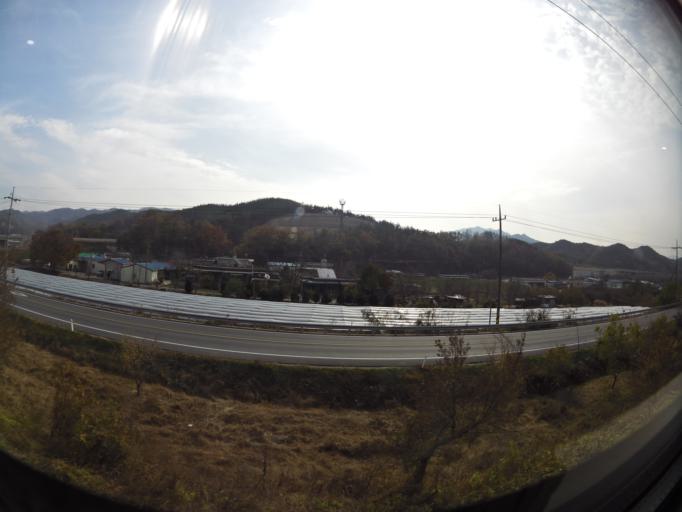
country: KR
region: Chungcheongbuk-do
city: Yong-dong
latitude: 36.1872
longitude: 127.8504
